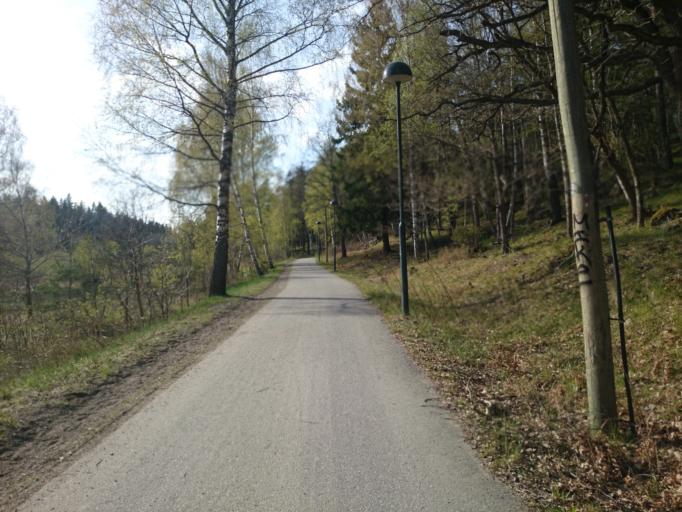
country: SE
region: Stockholm
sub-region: Stockholms Kommun
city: Arsta
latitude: 59.2286
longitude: 18.0565
